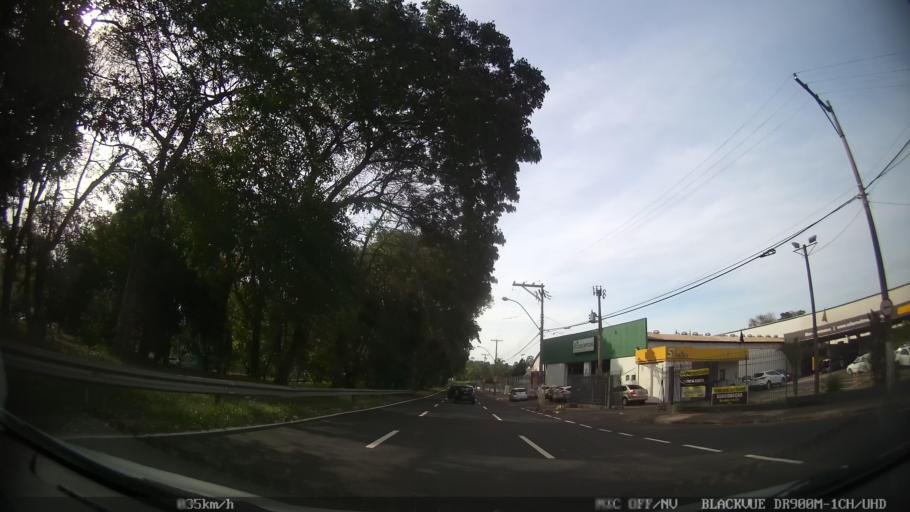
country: BR
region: Sao Paulo
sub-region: Piracicaba
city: Piracicaba
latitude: -22.7247
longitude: -47.6256
